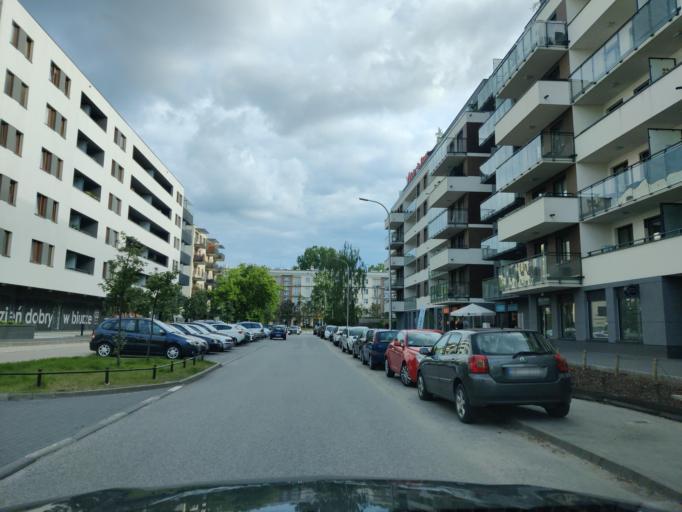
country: PL
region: Masovian Voivodeship
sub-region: Warszawa
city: Praga Poludnie
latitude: 52.2540
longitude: 21.0816
